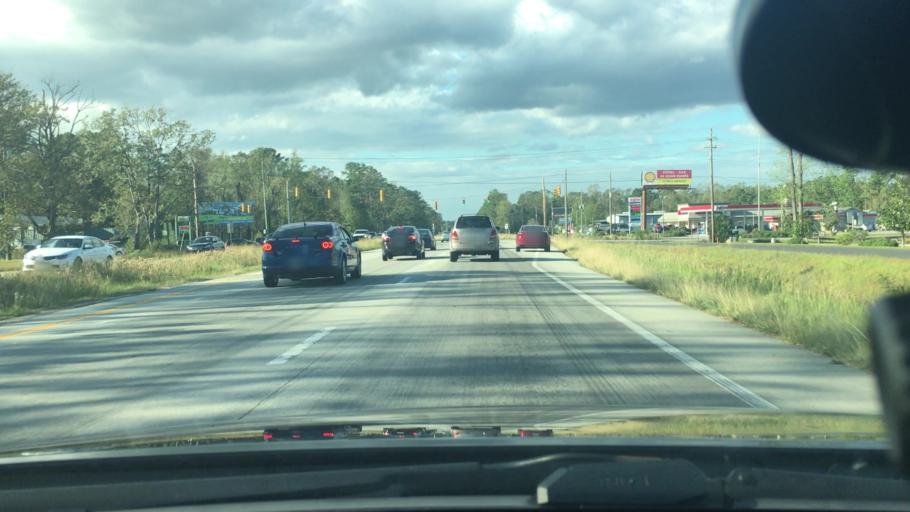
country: US
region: North Carolina
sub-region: Craven County
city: Fairfield Harbour
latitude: 35.0370
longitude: -77.0065
